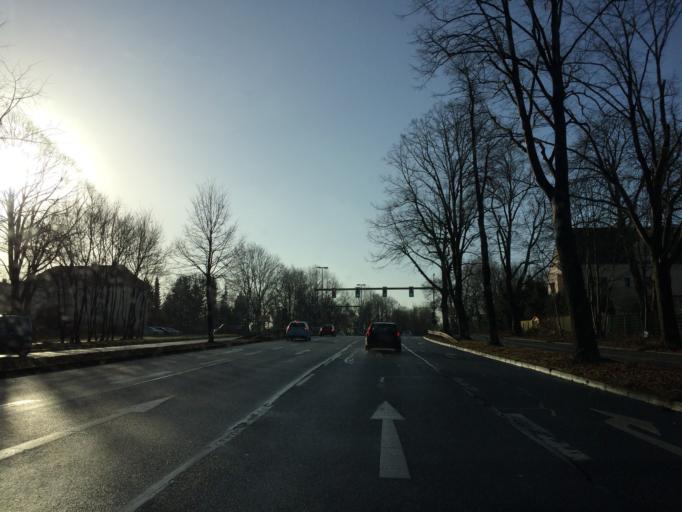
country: DE
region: North Rhine-Westphalia
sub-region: Regierungsbezirk Arnsberg
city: Bochum
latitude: 51.4478
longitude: 7.2262
